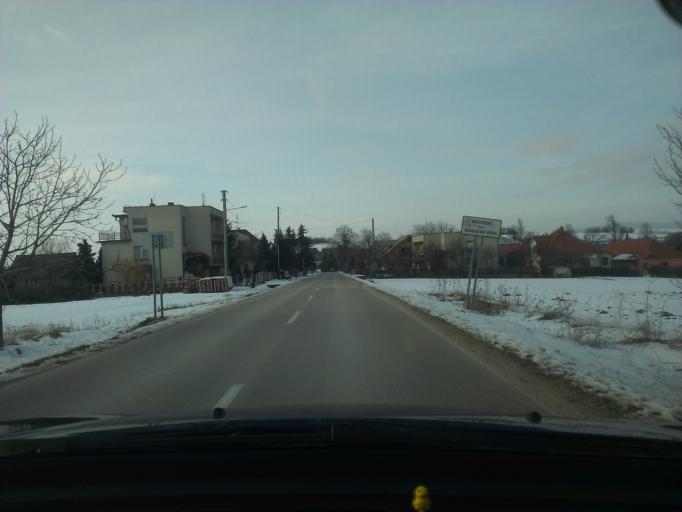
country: SK
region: Nitriansky
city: Stara Tura
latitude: 48.7335
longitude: 17.6597
